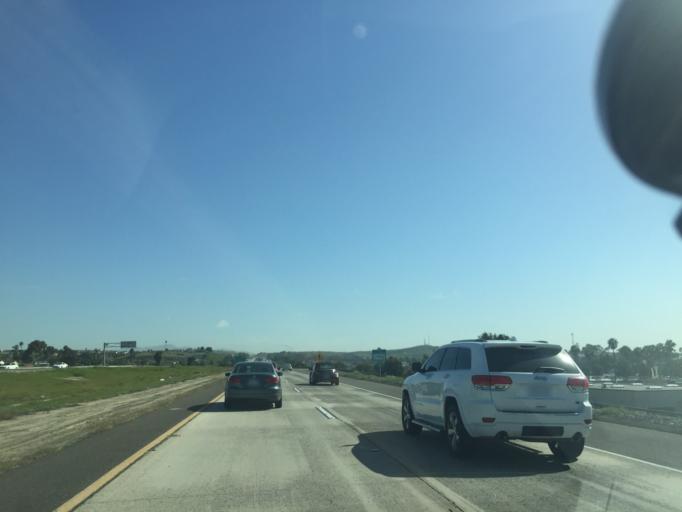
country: US
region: California
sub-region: San Diego County
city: Imperial Beach
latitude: 32.5682
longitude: -117.0618
